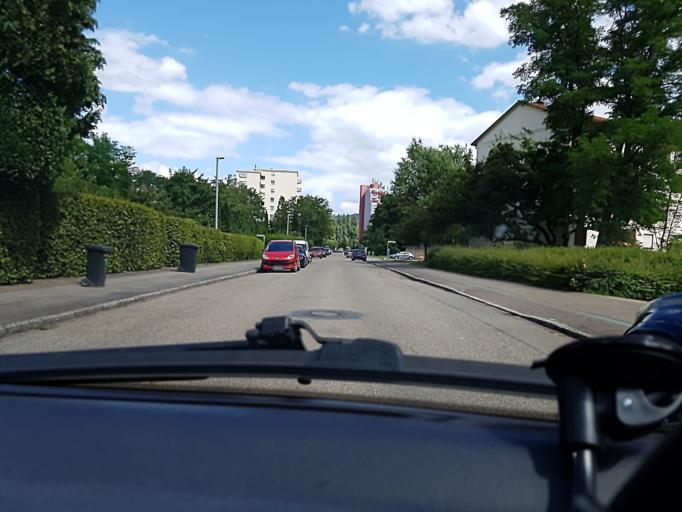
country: DE
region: Baden-Wuerttemberg
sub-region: Freiburg Region
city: Offenburg
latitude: 48.4670
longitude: 7.9222
